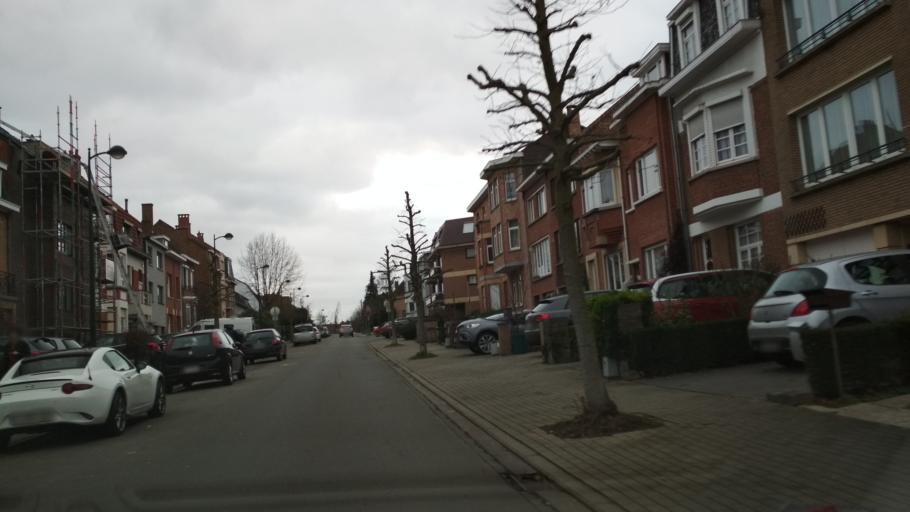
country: BE
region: Flanders
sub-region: Provincie Vlaams-Brabant
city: Hoeilaart
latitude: 50.8089
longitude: 4.4399
